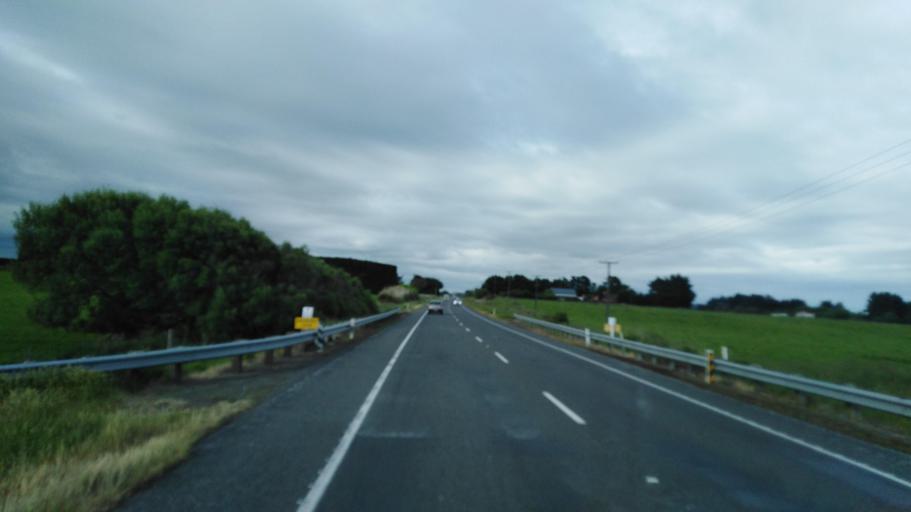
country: NZ
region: Manawatu-Wanganui
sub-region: Rangitikei District
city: Bulls
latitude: -40.2515
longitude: 175.3945
